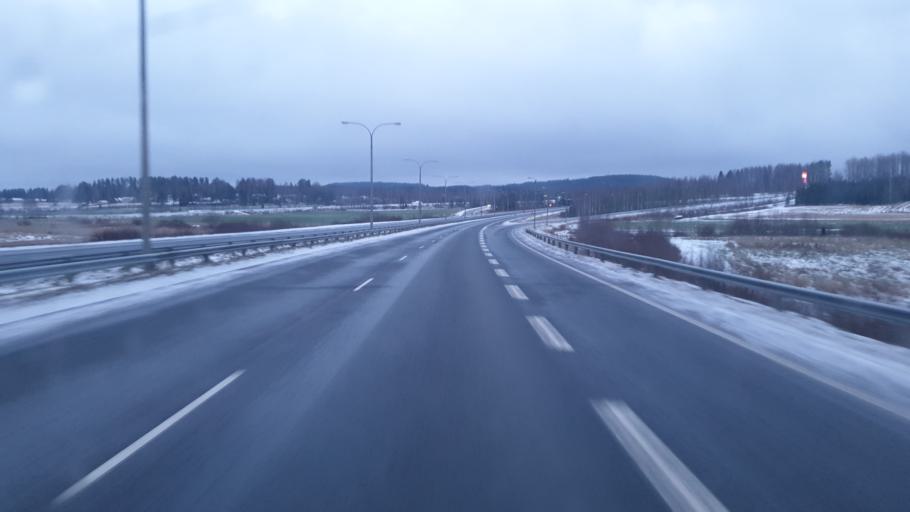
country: FI
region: Northern Savo
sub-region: Kuopio
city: Siilinjaervi
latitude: 62.9941
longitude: 27.6999
